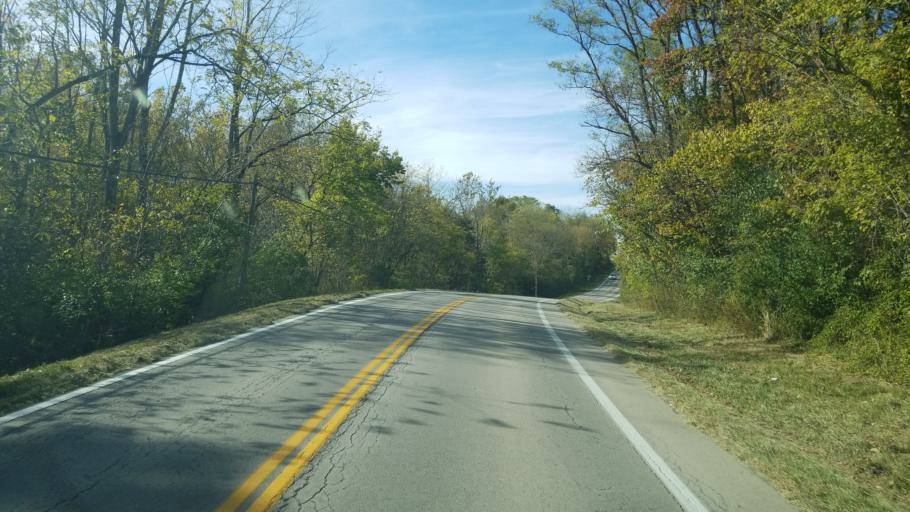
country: US
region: Ohio
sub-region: Clinton County
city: Blanchester
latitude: 39.3795
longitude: -83.9577
